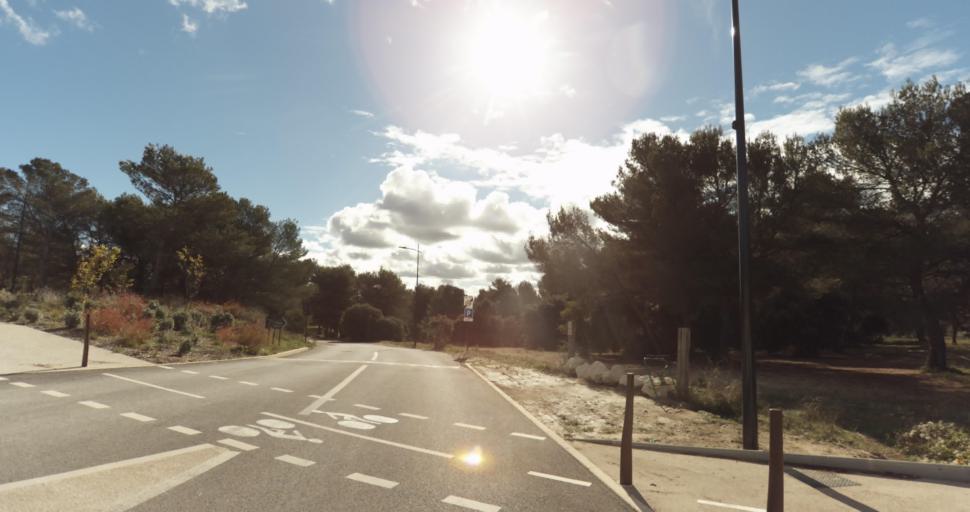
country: FR
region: Provence-Alpes-Cote d'Azur
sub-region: Departement des Bouches-du-Rhone
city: Venelles
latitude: 43.5952
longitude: 5.4920
